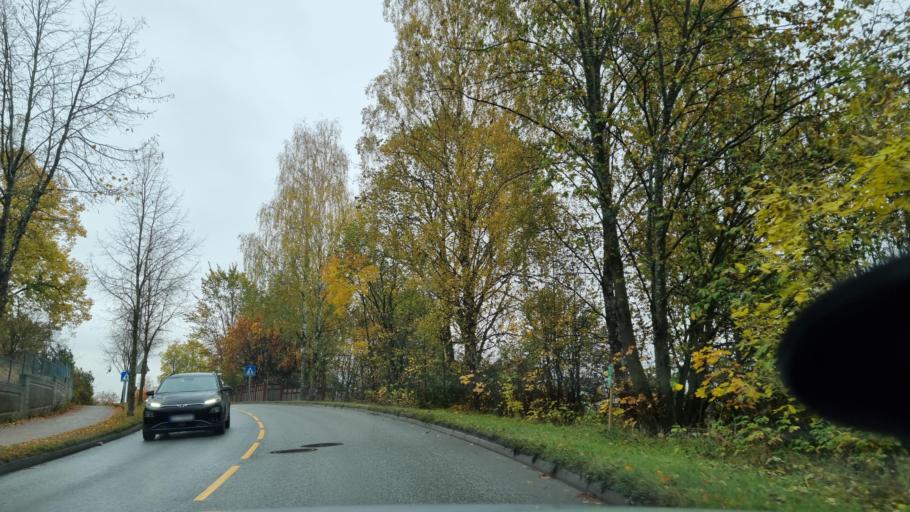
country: NO
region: Hedmark
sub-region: Hamar
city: Hamar
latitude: 60.8048
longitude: 11.0722
